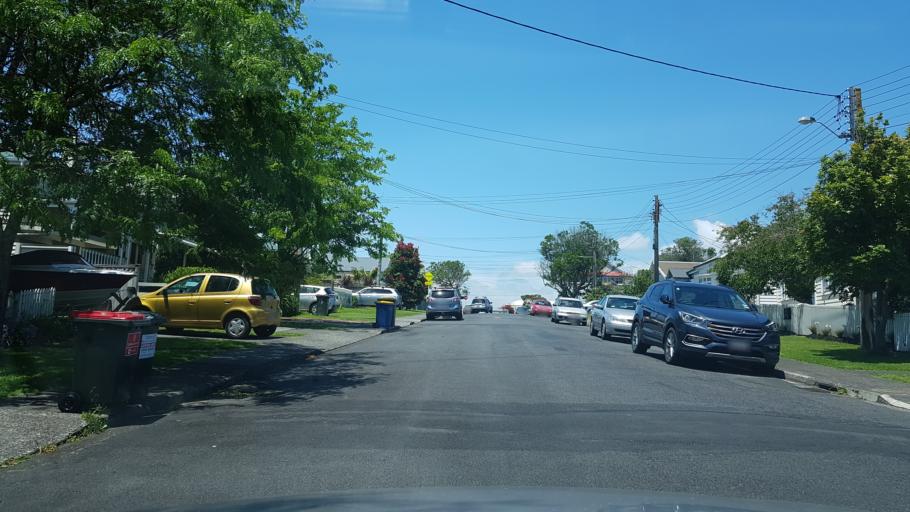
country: NZ
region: Auckland
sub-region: Auckland
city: Auckland
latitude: -36.8278
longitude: 174.7913
